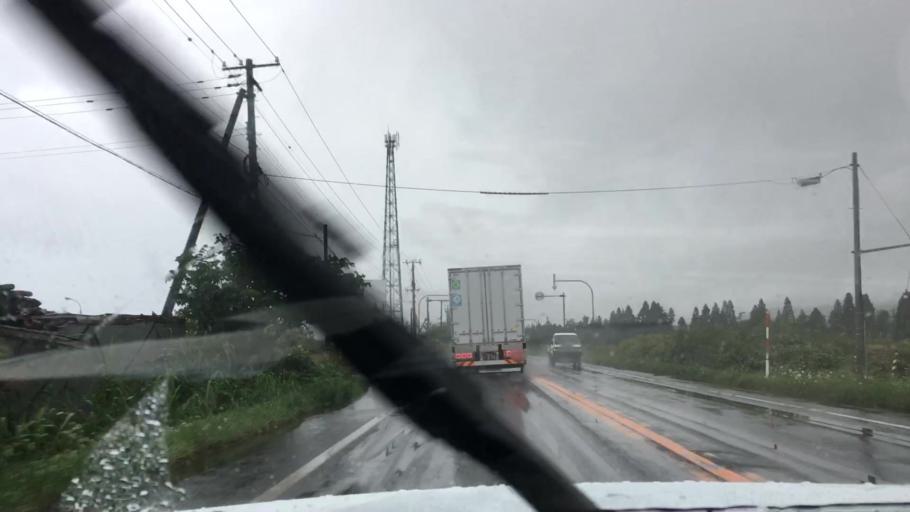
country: JP
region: Hokkaido
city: Niseko Town
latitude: 42.4737
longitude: 140.3456
